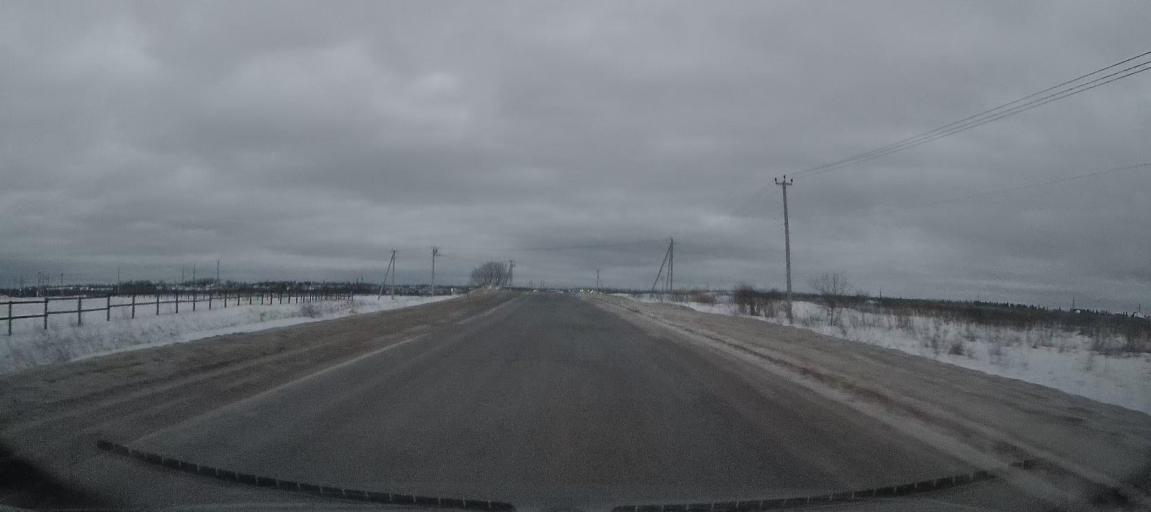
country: RU
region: Leningrad
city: Taytsy
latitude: 59.6895
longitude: 30.1369
